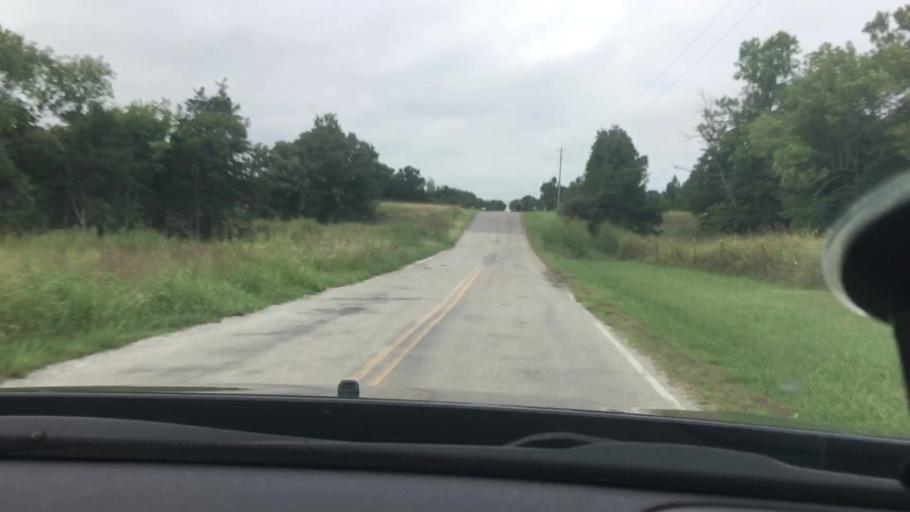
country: US
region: Oklahoma
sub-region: Pontotoc County
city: Byng
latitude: 34.8033
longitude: -96.5475
